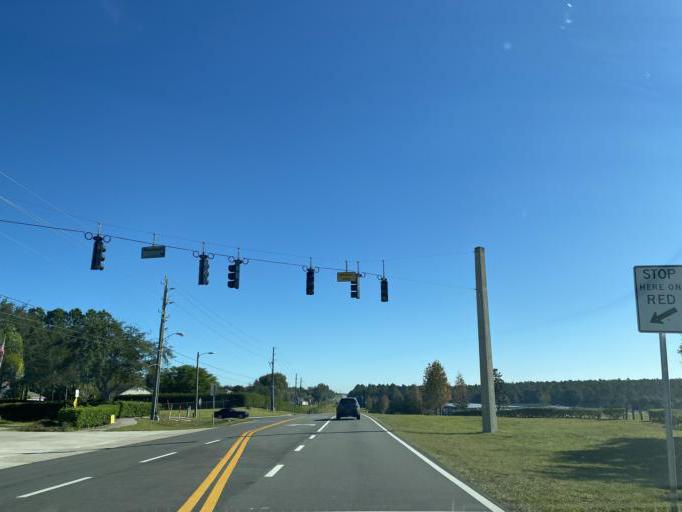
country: US
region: Florida
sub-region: Lake County
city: Clermont
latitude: 28.4998
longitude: -81.7156
